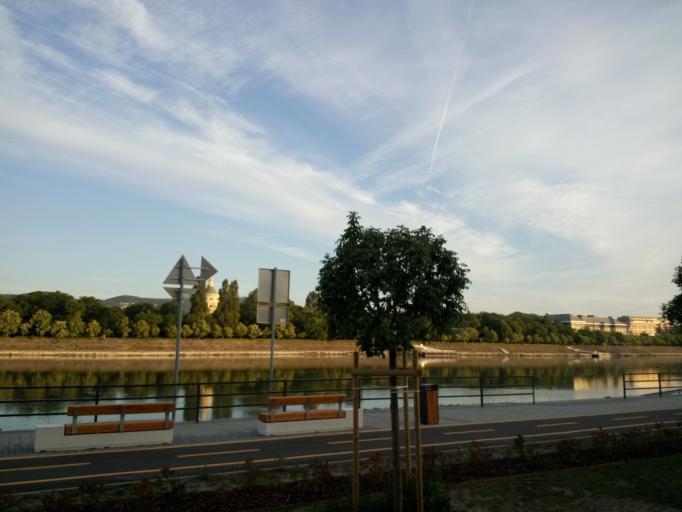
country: HU
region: Budapest
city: Budapest III. keruelet
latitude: 47.5279
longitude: 19.0554
